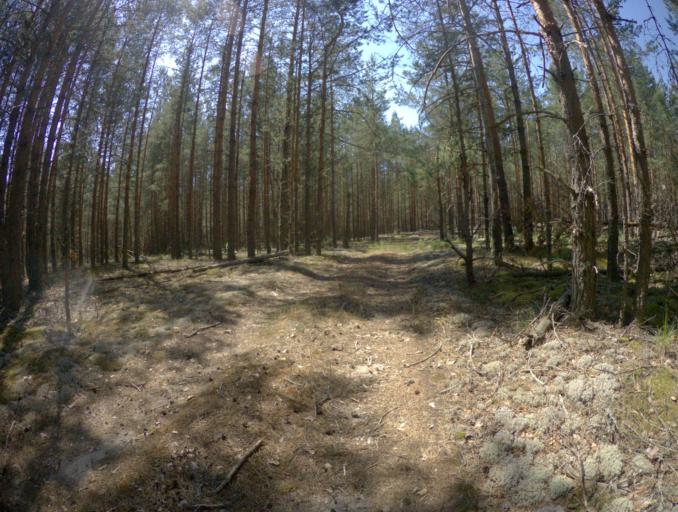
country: RU
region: Ivanovo
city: Talitsy
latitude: 56.3772
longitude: 42.3027
